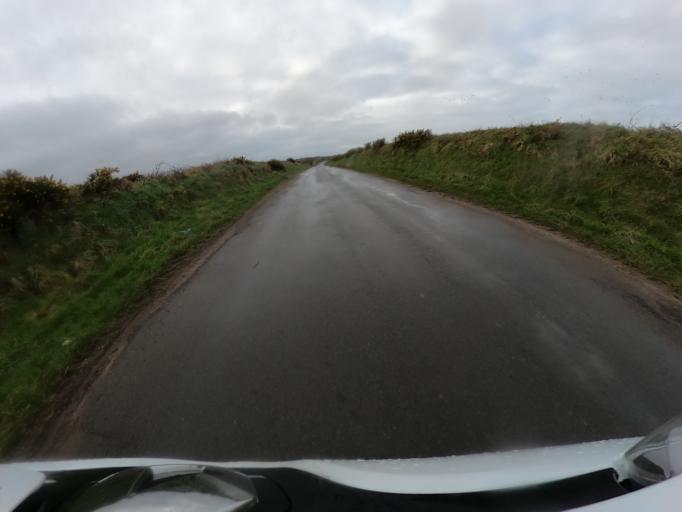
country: IM
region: Ramsey
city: Ramsey
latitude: 54.3631
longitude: -4.4633
